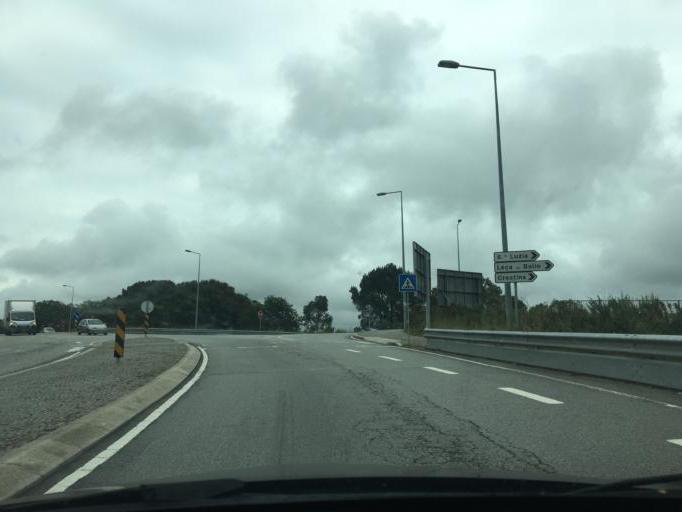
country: PT
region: Porto
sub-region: Maia
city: Gemunde
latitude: 41.2408
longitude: -8.6494
